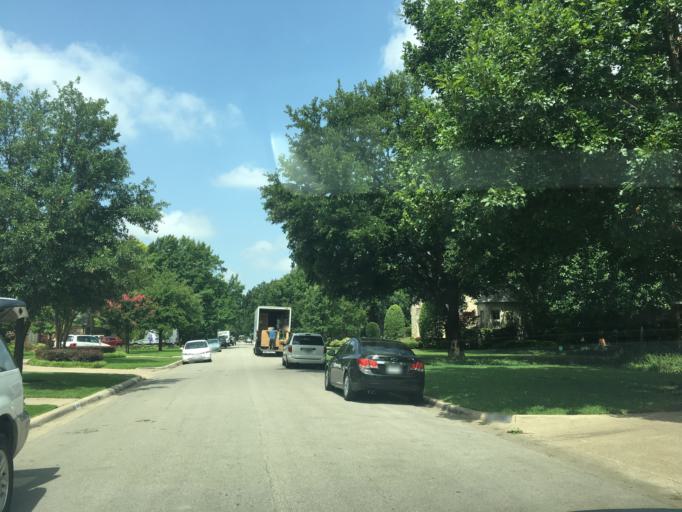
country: US
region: Texas
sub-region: Dallas County
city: University Park
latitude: 32.8758
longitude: -96.7981
